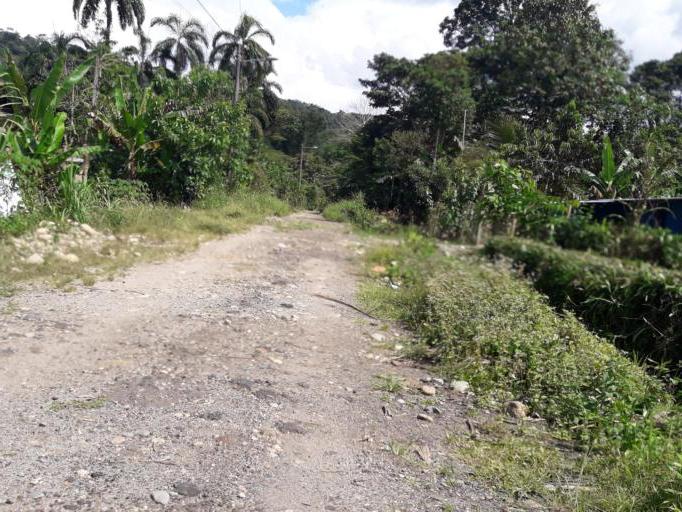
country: EC
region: Napo
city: Tena
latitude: -0.9550
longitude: -77.8250
